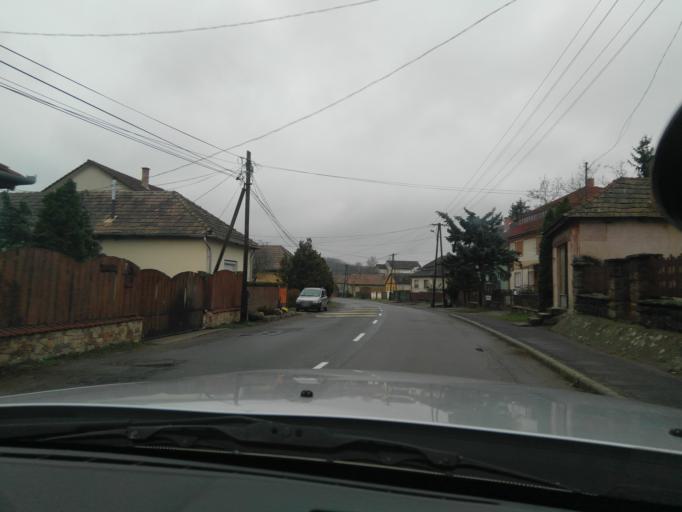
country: HU
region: Nograd
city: Matraterenye
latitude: 48.0292
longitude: 19.9488
